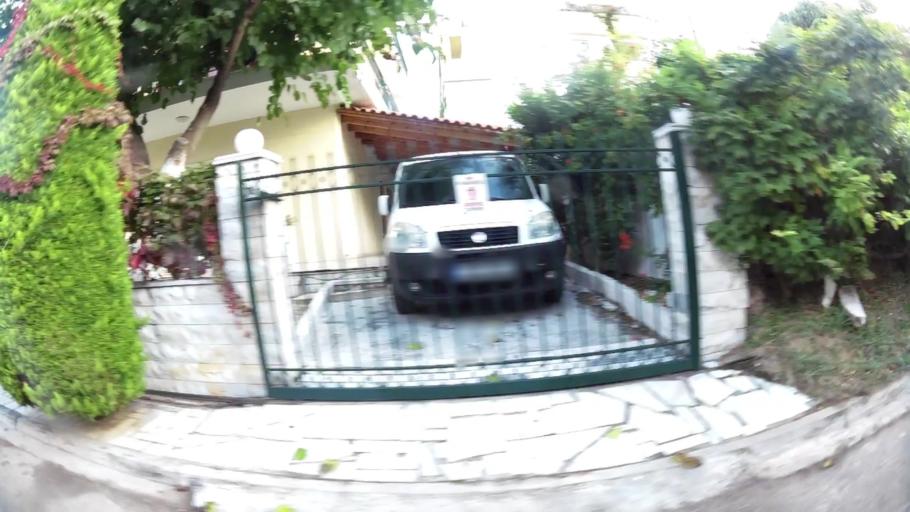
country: GR
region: Attica
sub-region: Nomarchia Athinas
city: Vrilissia
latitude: 38.0375
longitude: 23.8222
